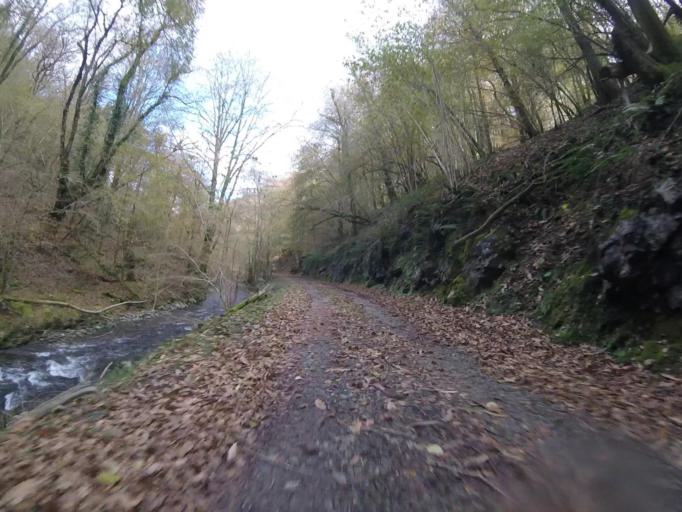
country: ES
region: Navarre
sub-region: Provincia de Navarra
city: Goizueta
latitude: 43.1958
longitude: -1.8046
